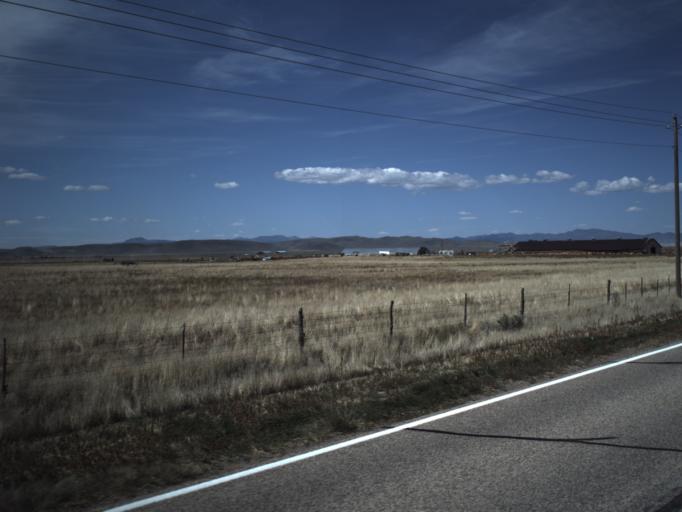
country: US
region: Utah
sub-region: Washington County
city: Enterprise
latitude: 37.6134
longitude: -113.6612
